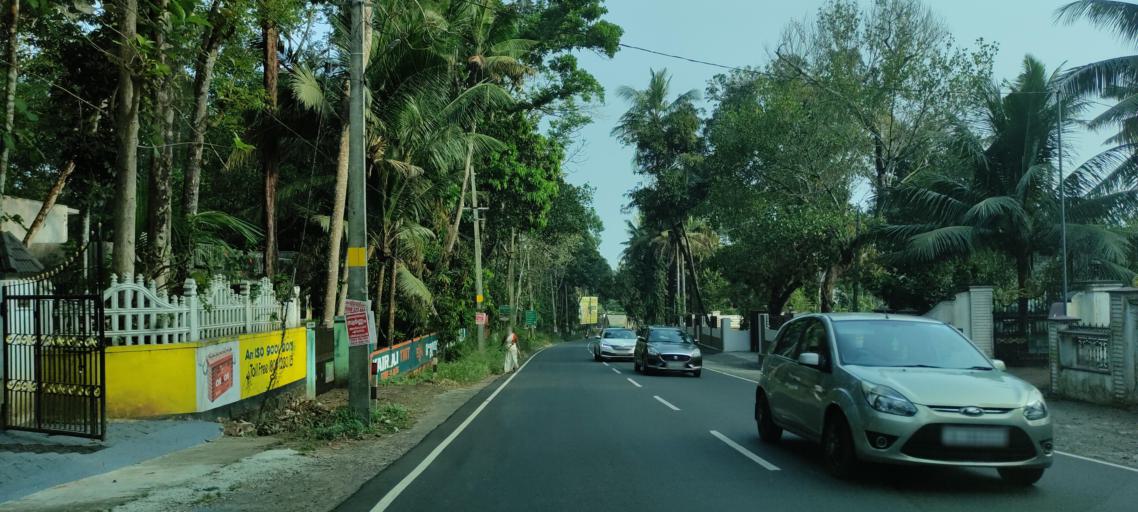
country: IN
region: Kerala
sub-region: Kottayam
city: Vaikam
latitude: 9.7586
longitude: 76.4951
